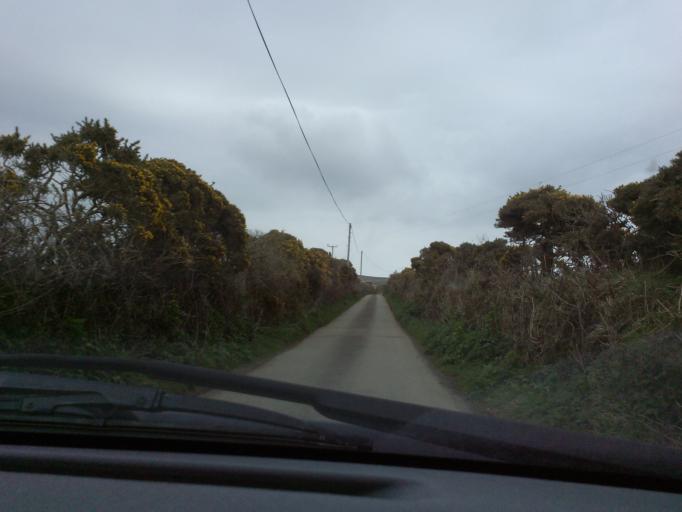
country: GB
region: England
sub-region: Cornwall
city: Saint Just
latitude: 50.1081
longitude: -5.6732
